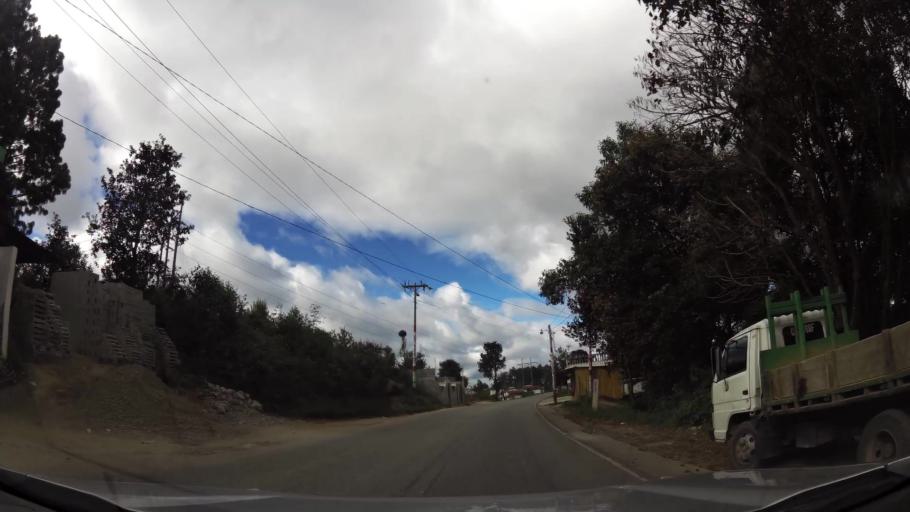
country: GT
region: Quiche
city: Chichicastenango
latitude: 14.8907
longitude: -91.1211
